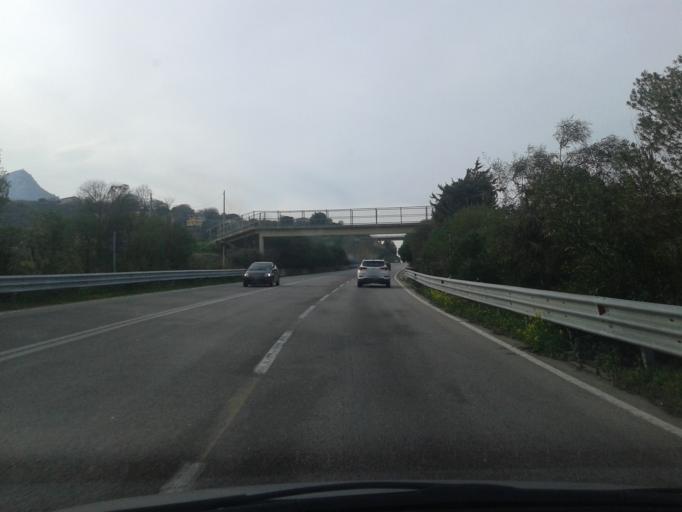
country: IT
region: Sicily
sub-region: Palermo
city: Giacalone
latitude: 38.0307
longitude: 13.2603
